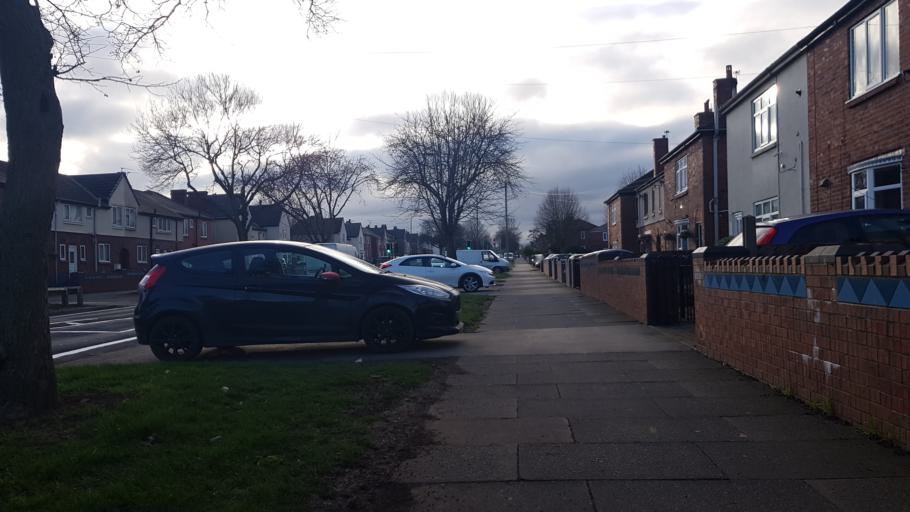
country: GB
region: England
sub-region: City and Borough of Wakefield
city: Pontefract
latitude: 53.7225
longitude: -1.3176
